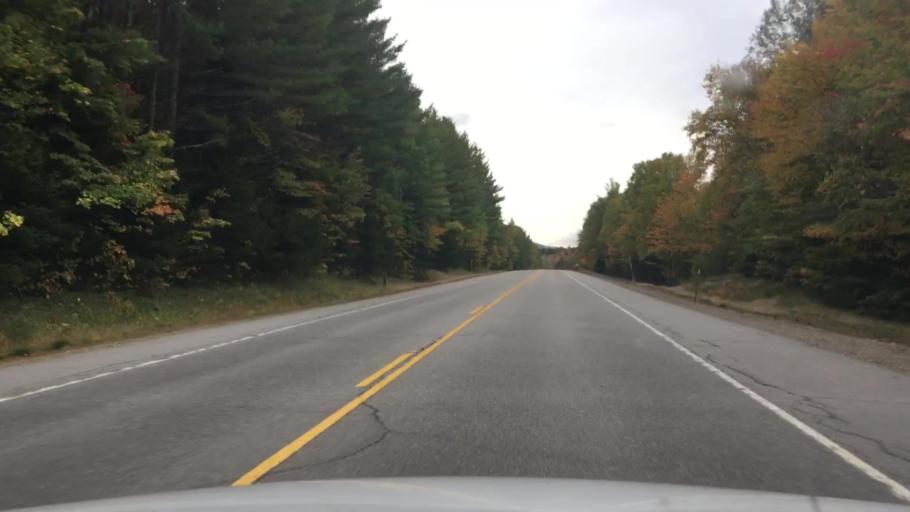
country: US
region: New Hampshire
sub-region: Coos County
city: Gorham
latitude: 44.3129
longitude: -71.2182
